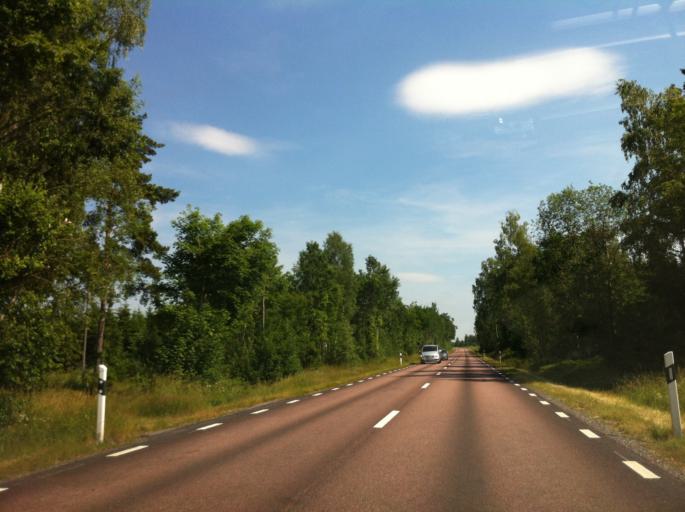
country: SE
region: Kalmar
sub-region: Nybro Kommun
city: Nybro
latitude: 56.7872
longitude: 15.8020
